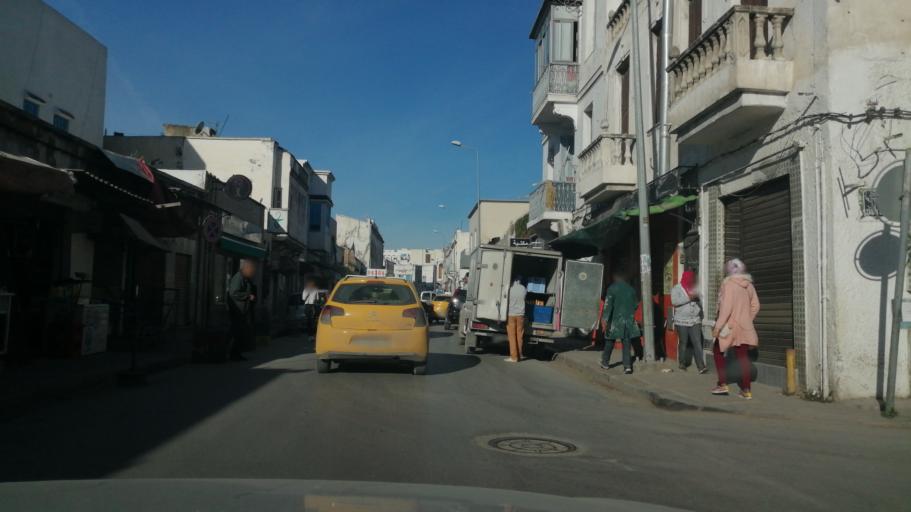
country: TN
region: Tunis
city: Tunis
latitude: 36.8069
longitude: 10.1635
